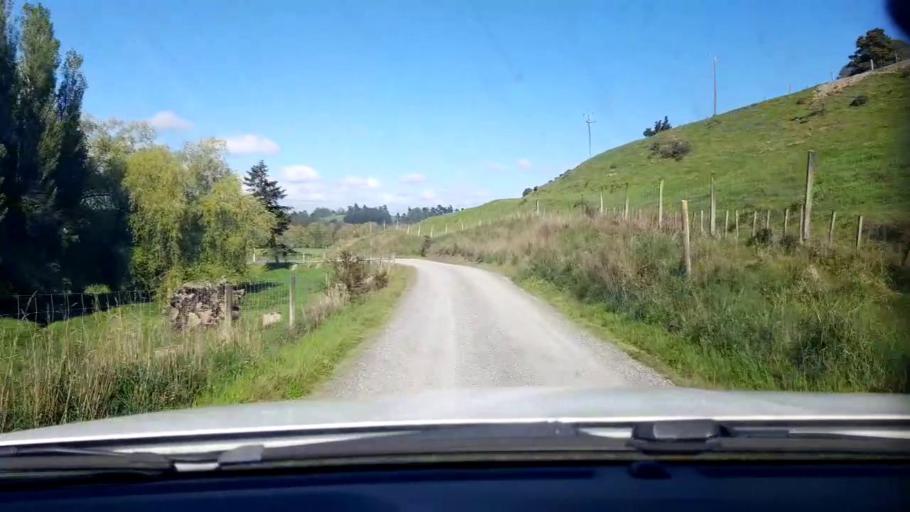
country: NZ
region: Otago
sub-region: Clutha District
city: Balclutha
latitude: -46.2231
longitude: 169.7337
